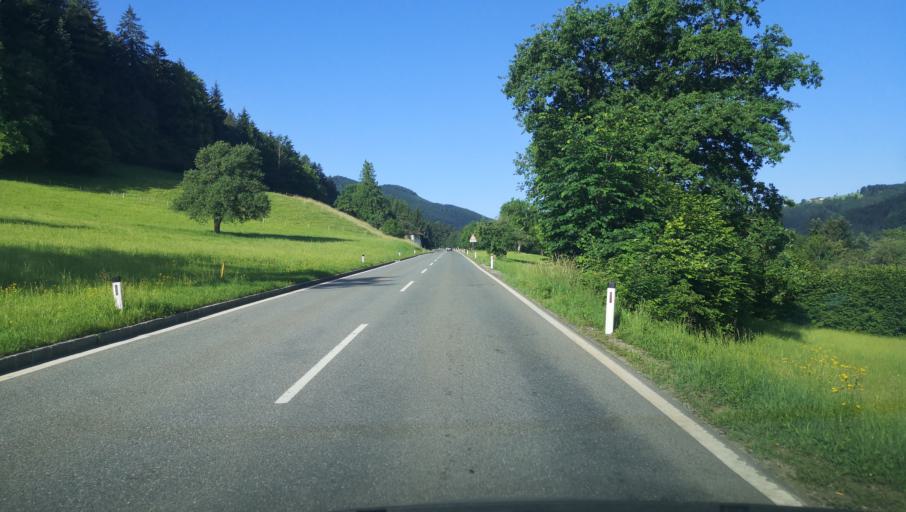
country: AT
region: Lower Austria
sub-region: Politischer Bezirk Scheibbs
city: Gresten
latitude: 47.9847
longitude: 15.0131
